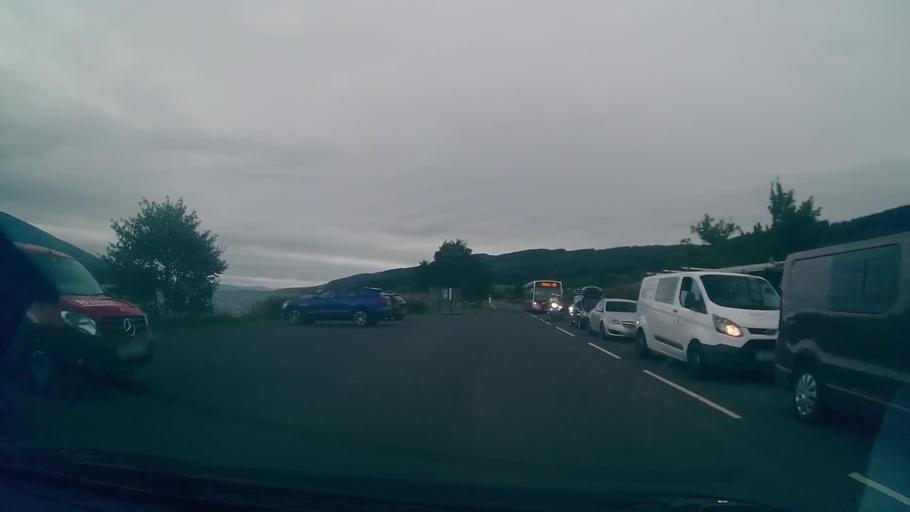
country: GB
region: Scotland
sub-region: Argyll and Bute
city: Port Bannatyne
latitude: 55.9206
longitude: -5.1588
